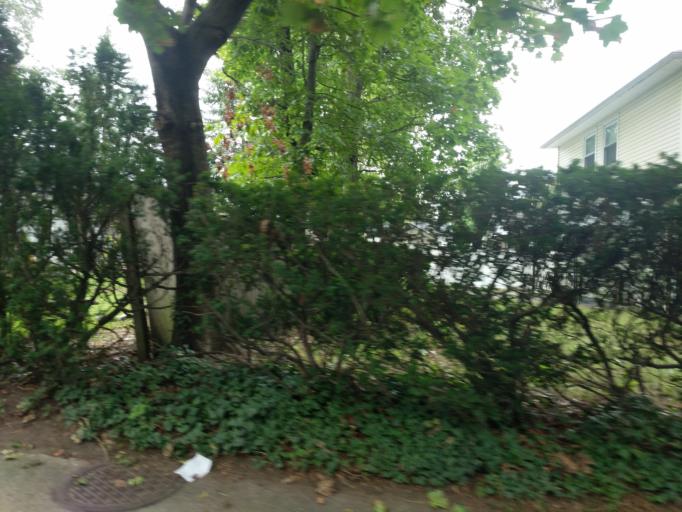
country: US
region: New York
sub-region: Nassau County
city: Malverne
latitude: 40.6767
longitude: -73.6769
